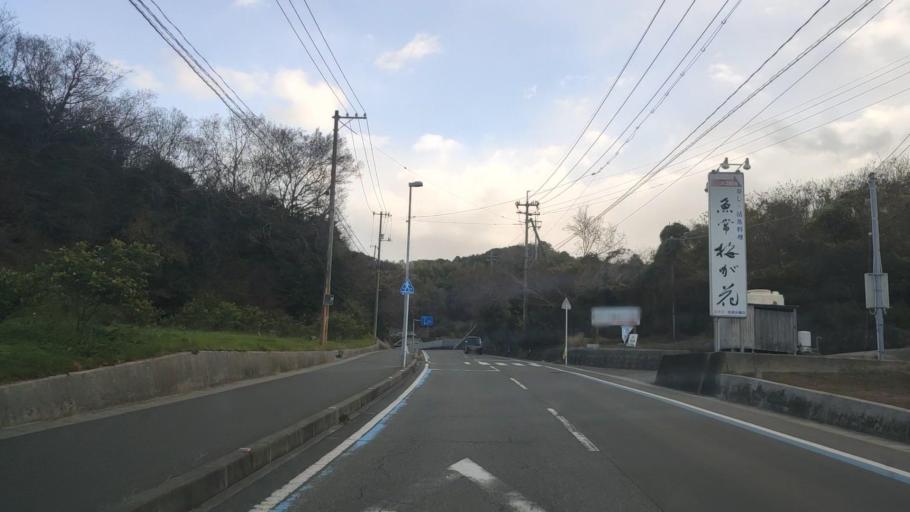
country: JP
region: Hiroshima
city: Innoshima
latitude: 34.2016
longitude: 133.1039
